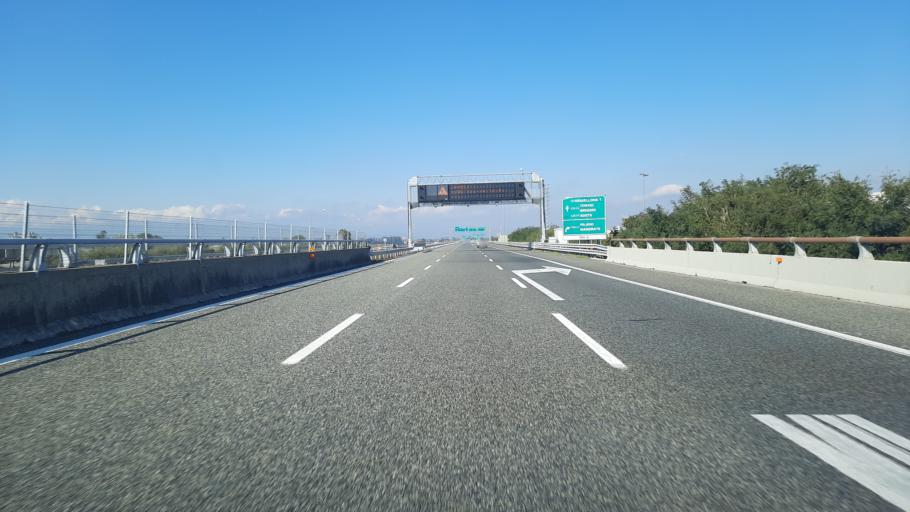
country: IT
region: Piedmont
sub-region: Provincia di Novara
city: Biandrate
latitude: 45.4571
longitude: 8.4534
